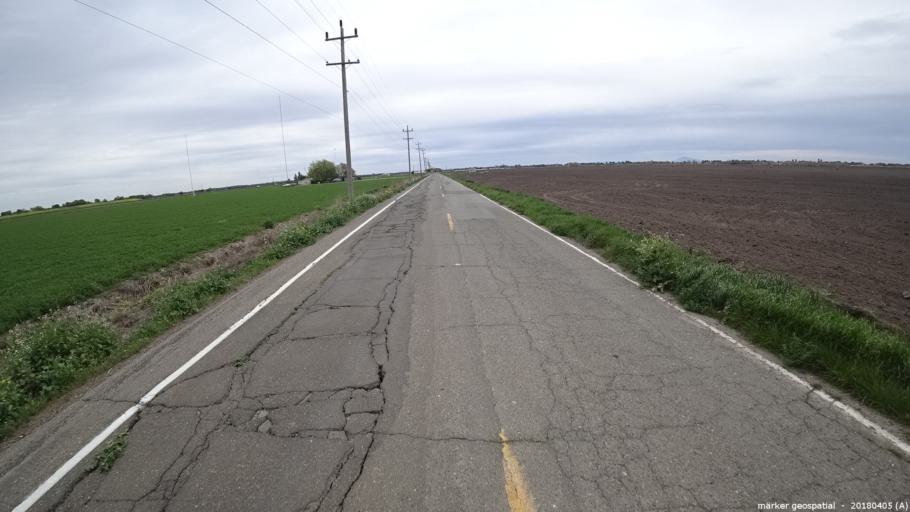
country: US
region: California
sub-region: Sacramento County
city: Walnut Grove
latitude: 38.2949
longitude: -121.5174
